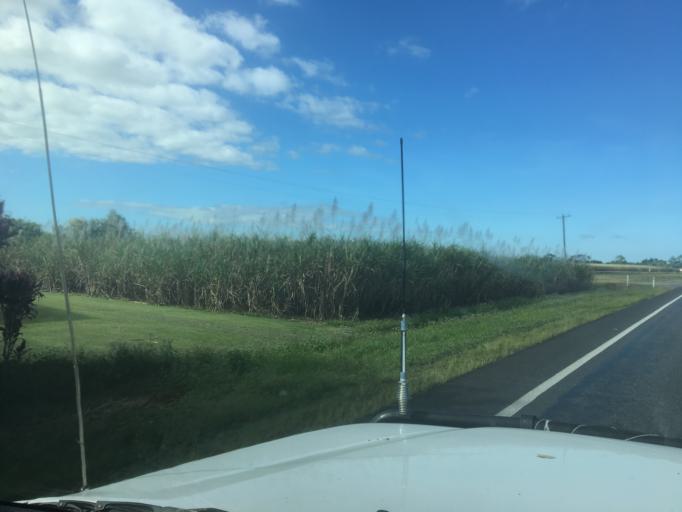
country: AU
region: Queensland
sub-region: Cassowary Coast
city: Innisfail
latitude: -17.3034
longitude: 145.9278
